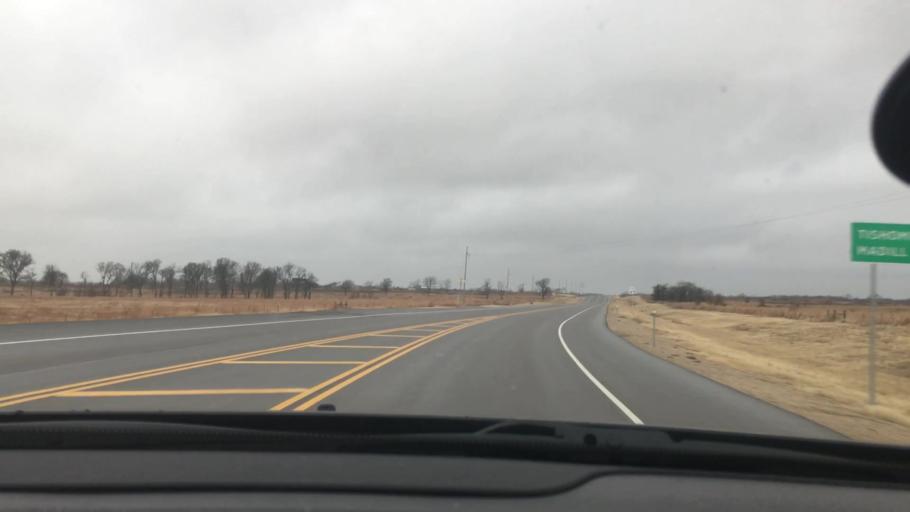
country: US
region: Oklahoma
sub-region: Johnston County
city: Tishomingo
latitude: 34.3458
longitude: -96.6373
